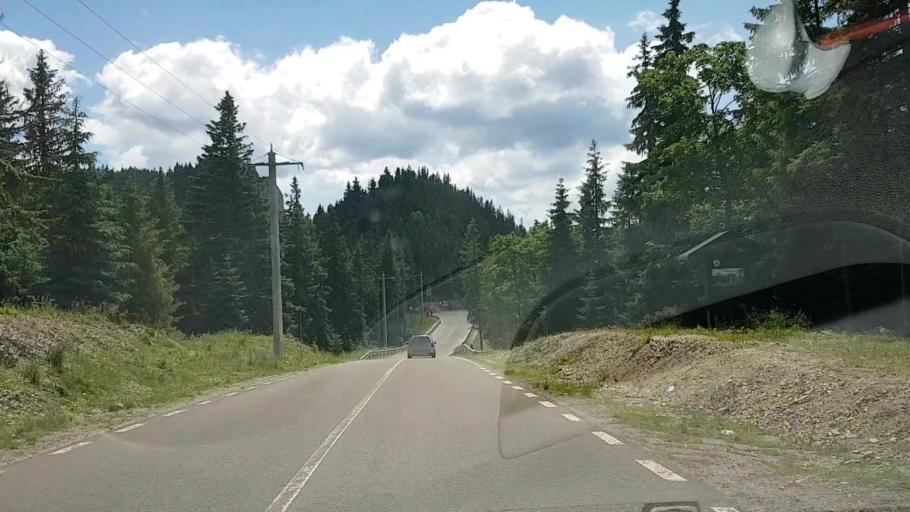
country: RO
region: Suceava
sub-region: Municipiul Campulung Moldovenesc
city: Campulung Moldovenesc
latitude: 47.4524
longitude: 25.5501
